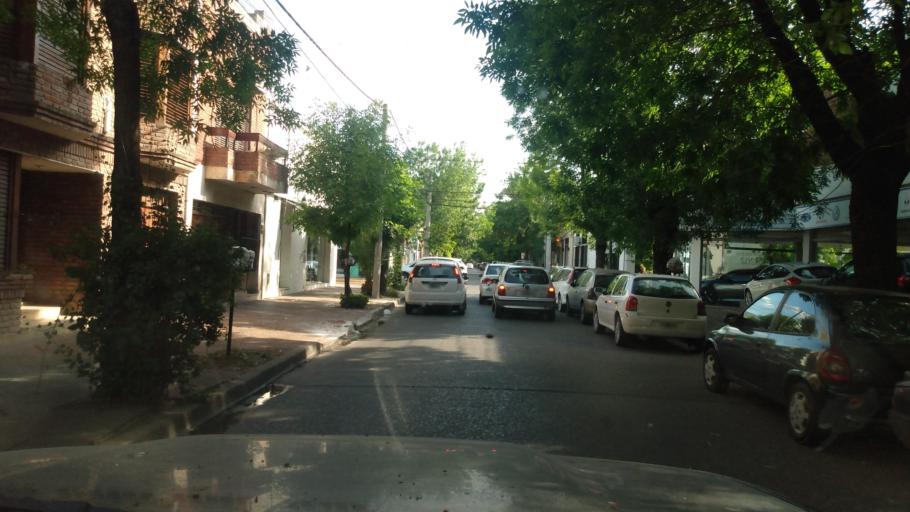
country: AR
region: Buenos Aires
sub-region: Partido de Lujan
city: Lujan
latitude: -34.5635
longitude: -59.1124
